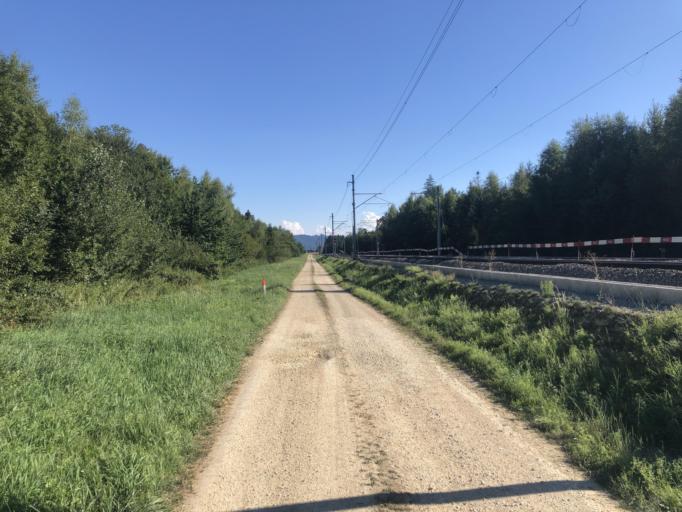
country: CH
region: Bern
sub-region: Bern-Mittelland District
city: Jegenstorf
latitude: 47.0673
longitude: 7.5072
